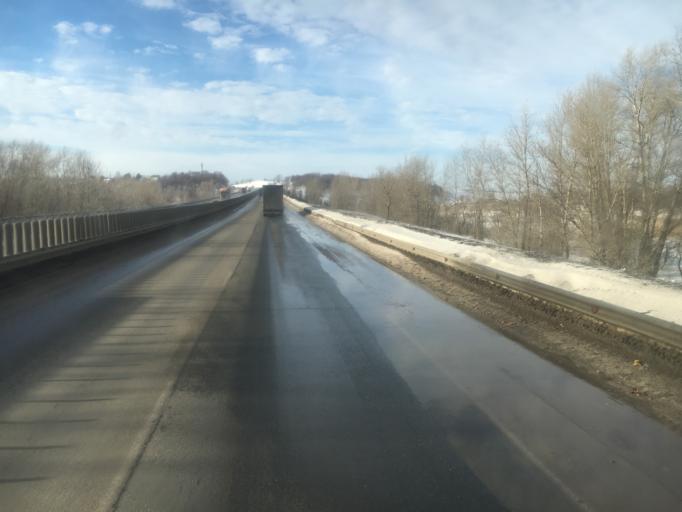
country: RU
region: Samara
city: Mirnyy
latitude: 53.4424
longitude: 50.2721
